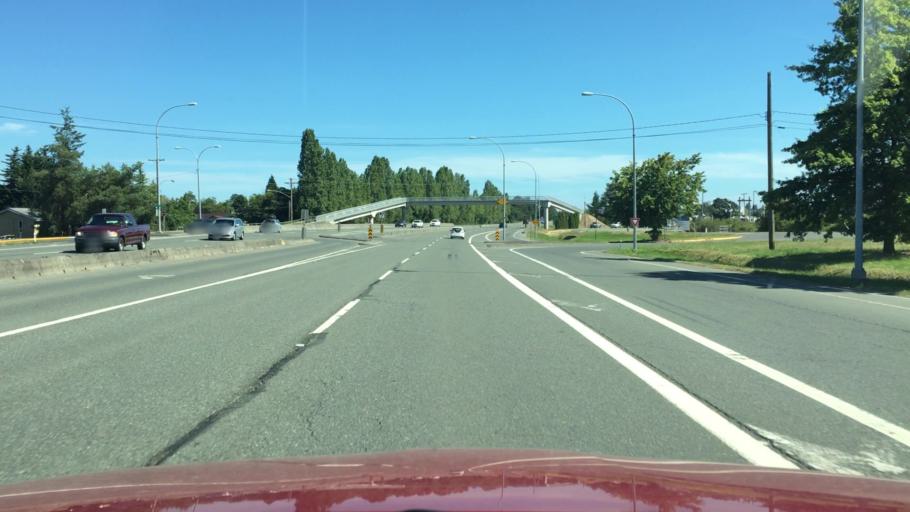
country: CA
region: British Columbia
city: North Saanich
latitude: 48.6637
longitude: -123.4183
